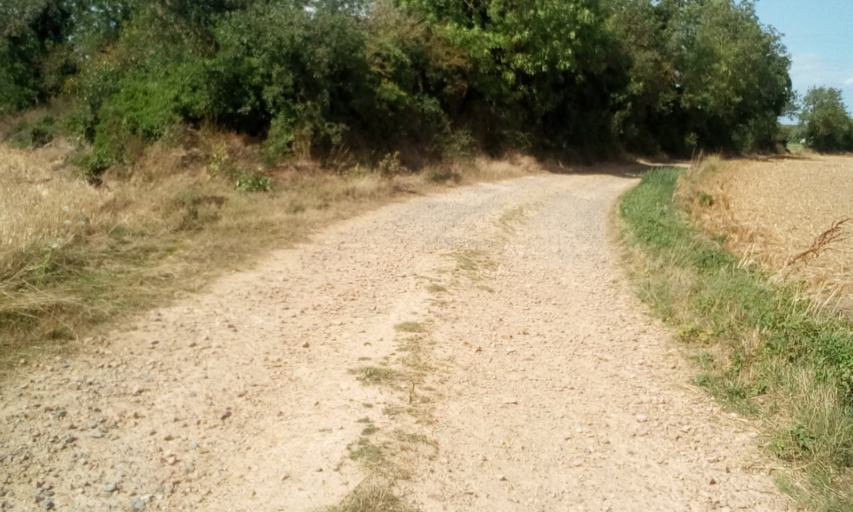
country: FR
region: Lower Normandy
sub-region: Departement du Calvados
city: Bellengreville
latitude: 49.1027
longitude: -0.2269
